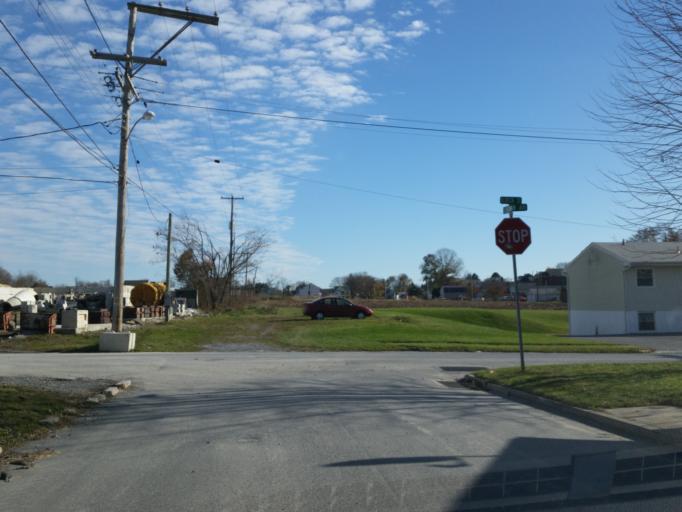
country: US
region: Pennsylvania
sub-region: Lebanon County
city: Annville
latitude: 40.3327
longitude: -76.5107
